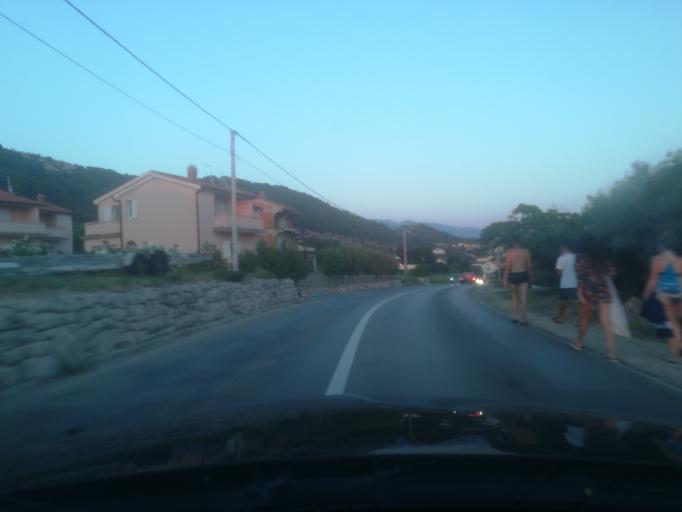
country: HR
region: Primorsko-Goranska
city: Banjol
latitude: 44.7446
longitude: 14.7933
